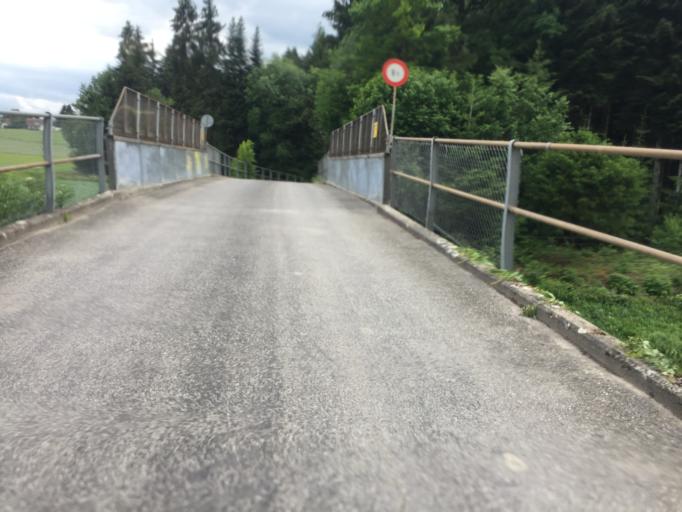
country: CH
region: Bern
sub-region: Bern-Mittelland District
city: Rubigen
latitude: 46.9240
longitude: 7.5241
